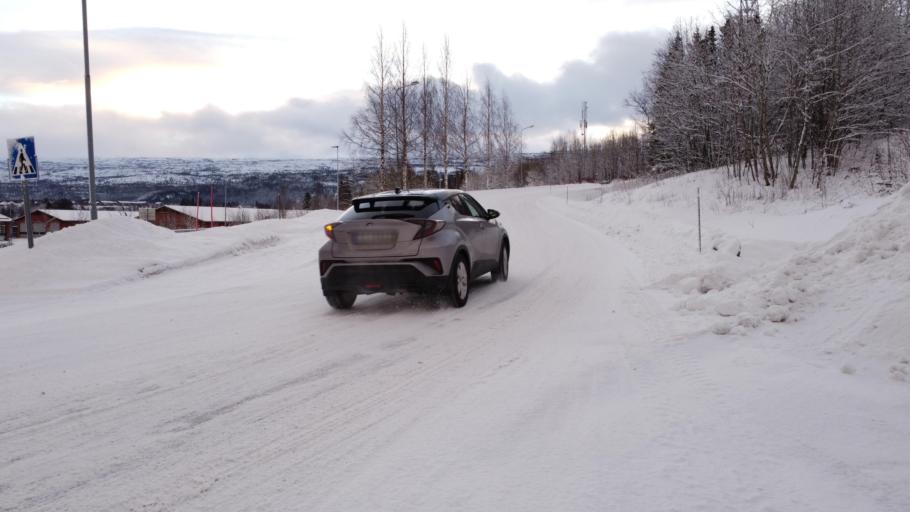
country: NO
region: Nordland
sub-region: Rana
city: Mo i Rana
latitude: 66.3281
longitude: 14.1579
